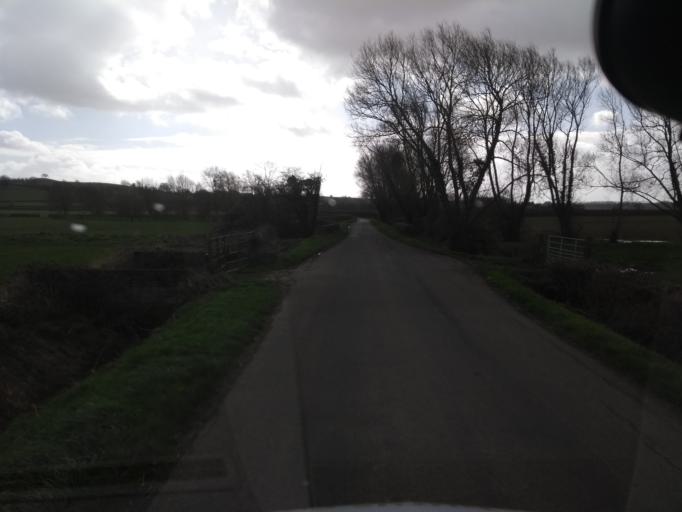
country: GB
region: England
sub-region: Somerset
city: Curry Rivel
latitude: 50.9838
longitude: -2.8489
